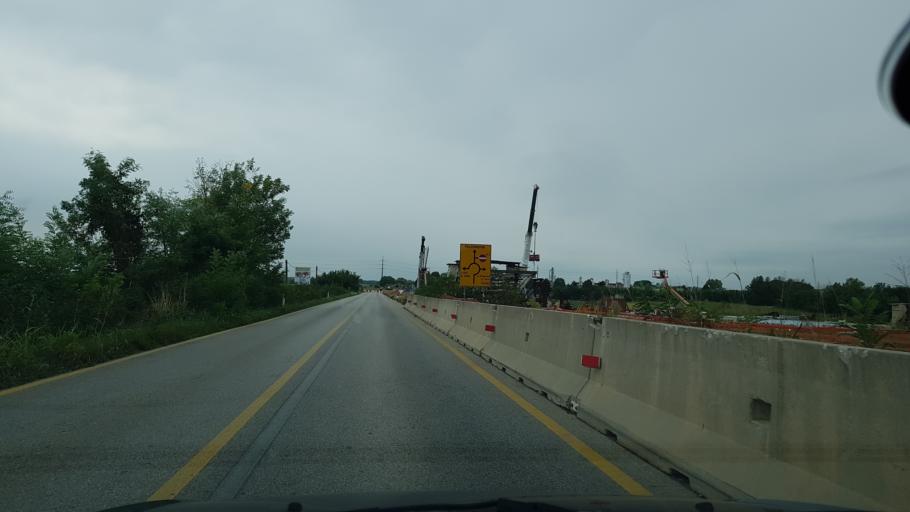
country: IT
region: Friuli Venezia Giulia
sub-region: Provincia di Udine
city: San Vito al Torre
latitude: 45.9235
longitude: 13.3764
